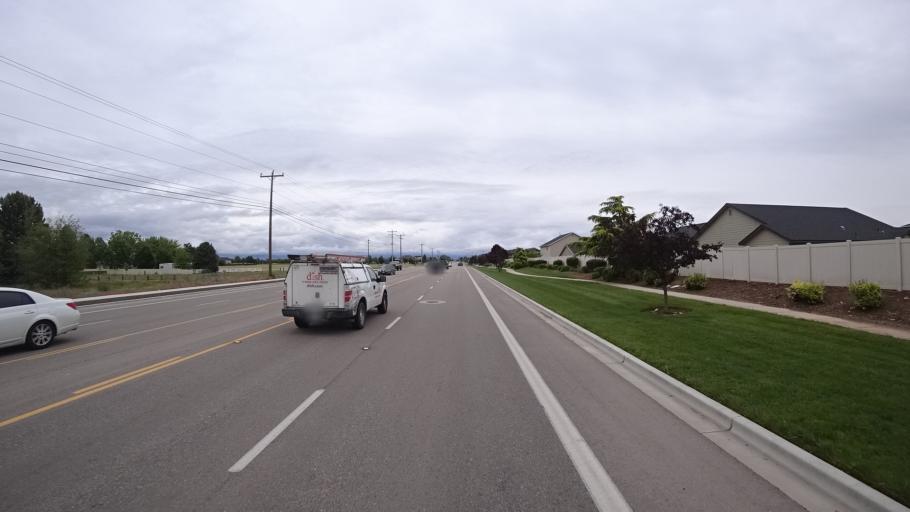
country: US
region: Idaho
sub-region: Ada County
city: Meridian
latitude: 43.6338
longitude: -116.4083
